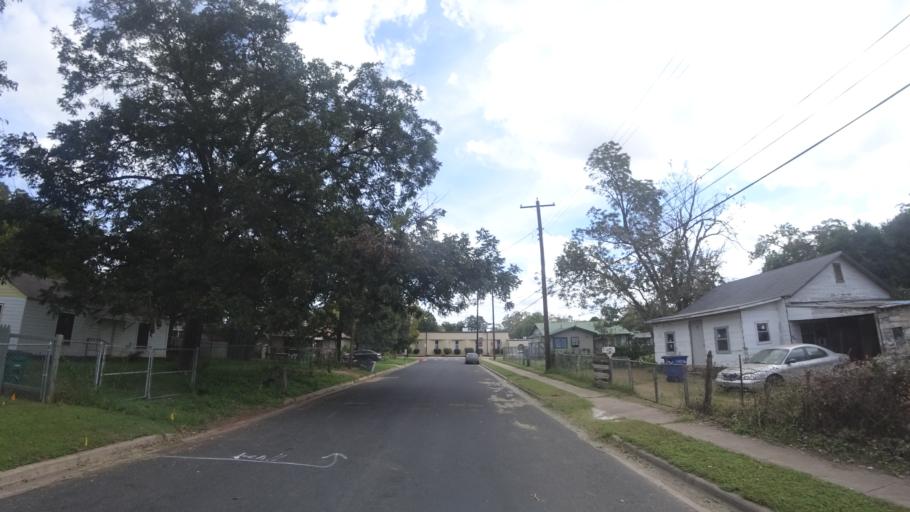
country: US
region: Texas
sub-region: Travis County
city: Austin
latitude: 30.2642
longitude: -97.7000
